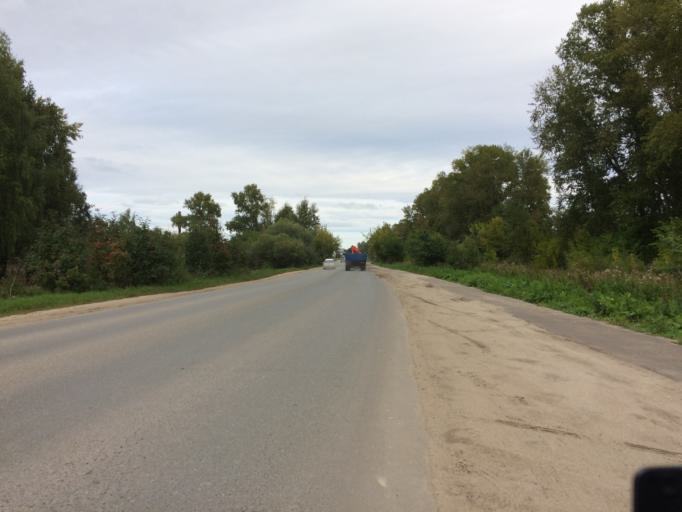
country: RU
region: Mariy-El
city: Yoshkar-Ola
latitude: 56.6491
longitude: 47.9558
